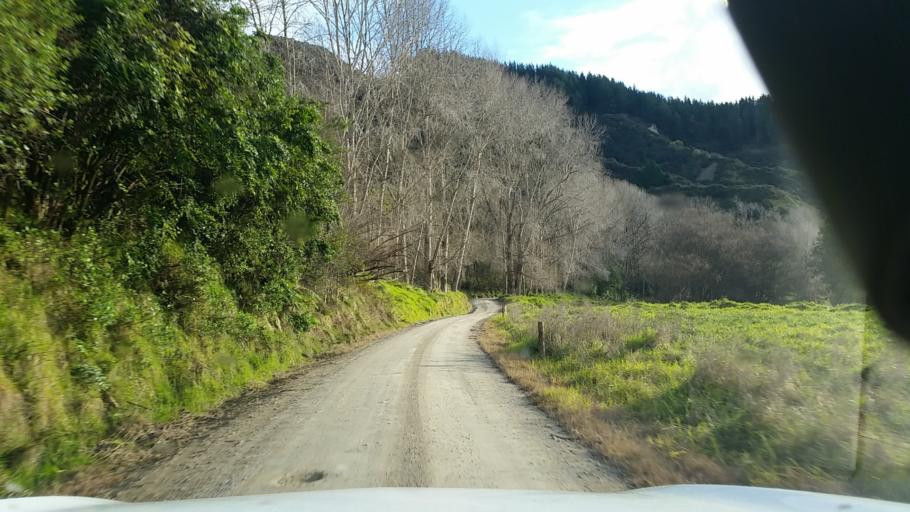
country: NZ
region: Taranaki
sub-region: South Taranaki District
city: Patea
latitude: -39.5724
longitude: 174.8168
